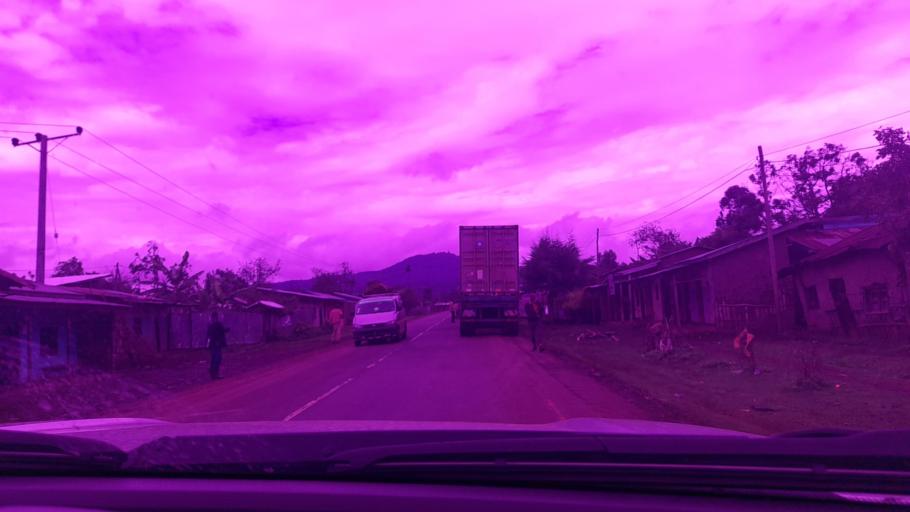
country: ET
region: Oromiya
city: Jima
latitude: 7.5564
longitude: 36.6207
